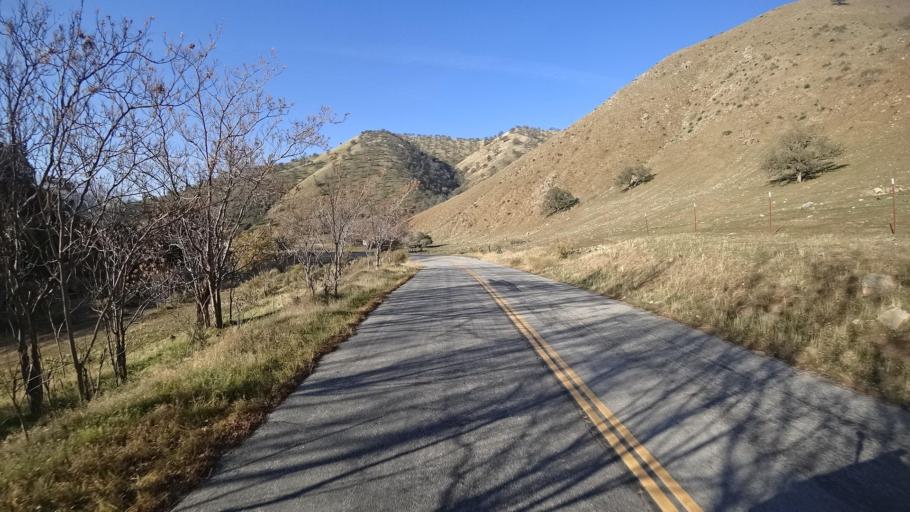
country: US
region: California
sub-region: Kern County
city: Bear Valley Springs
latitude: 35.3091
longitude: -118.5815
